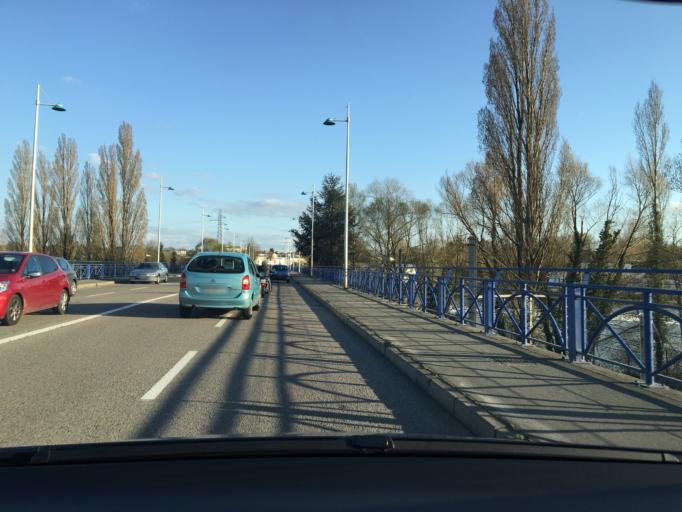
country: FR
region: Franche-Comte
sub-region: Departement du Doubs
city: Montbeliard
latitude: 47.5064
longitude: 6.8102
